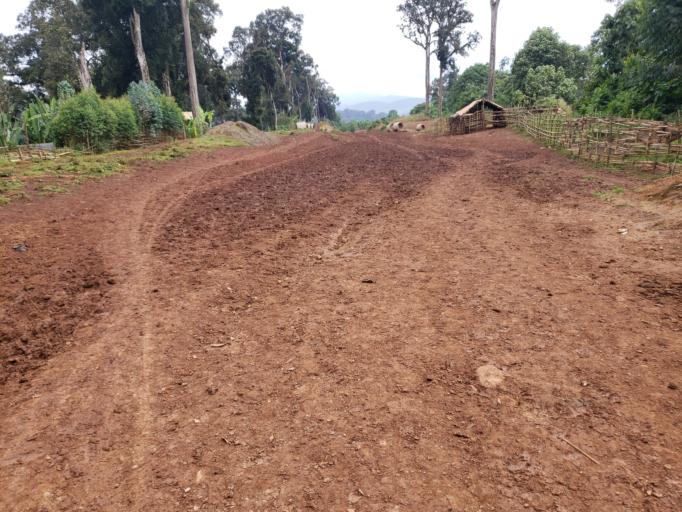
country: ET
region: Oromiya
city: Dodola
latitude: 6.5519
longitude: 39.4226
